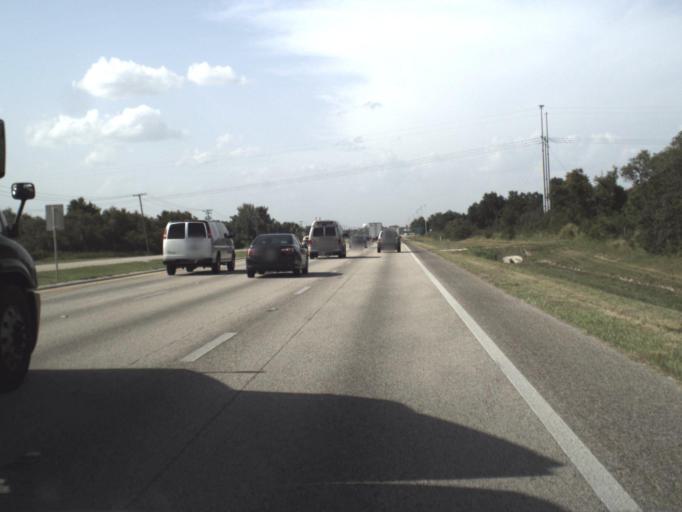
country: US
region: Florida
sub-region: Polk County
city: Lake Wales
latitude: 27.9179
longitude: -81.6044
